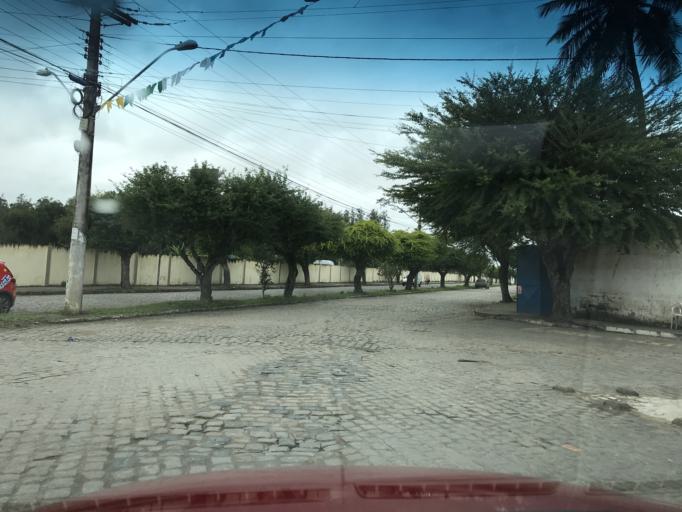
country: BR
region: Bahia
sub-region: Cruz Das Almas
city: Cruz das Almas
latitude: -12.6615
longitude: -39.1013
